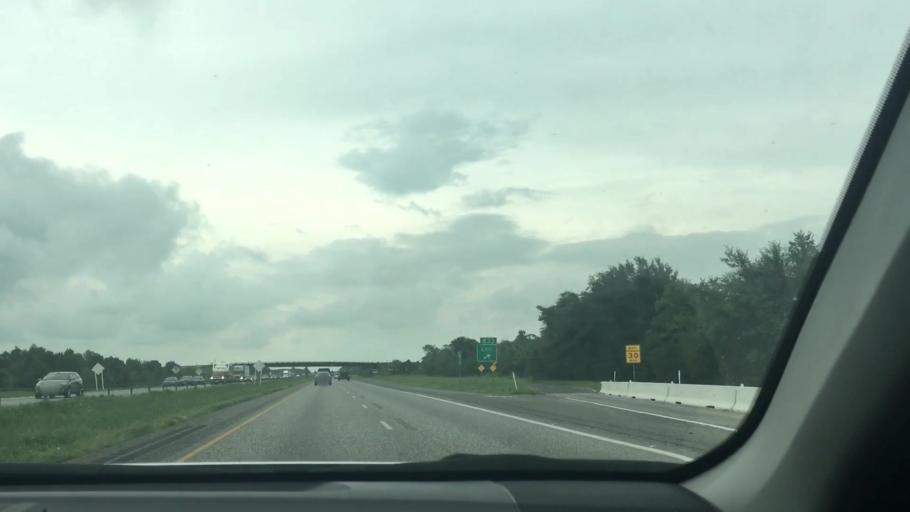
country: US
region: Texas
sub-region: Chambers County
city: Winnie
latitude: 29.8757
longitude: -94.3374
